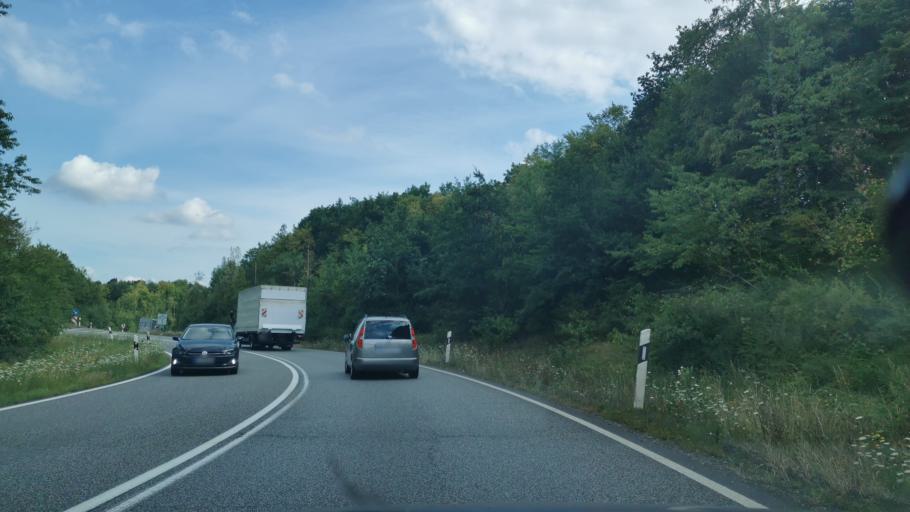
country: DE
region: Rheinland-Pfalz
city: Mayen
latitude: 50.3174
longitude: 7.2397
